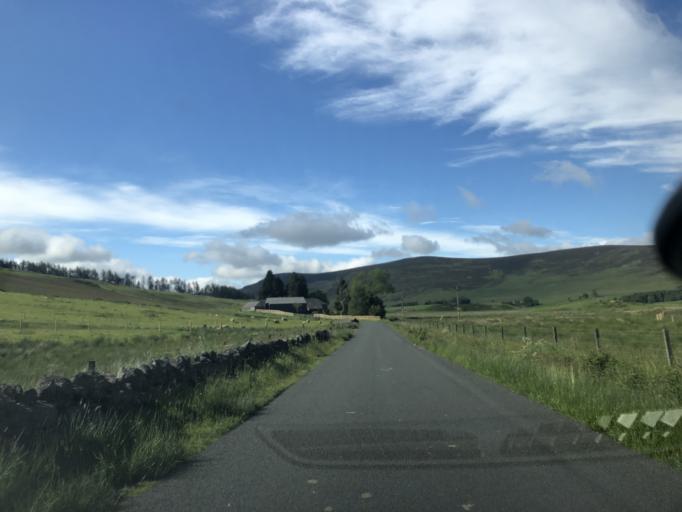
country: GB
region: Scotland
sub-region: Angus
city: Kirriemuir
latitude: 56.8091
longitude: -3.0343
